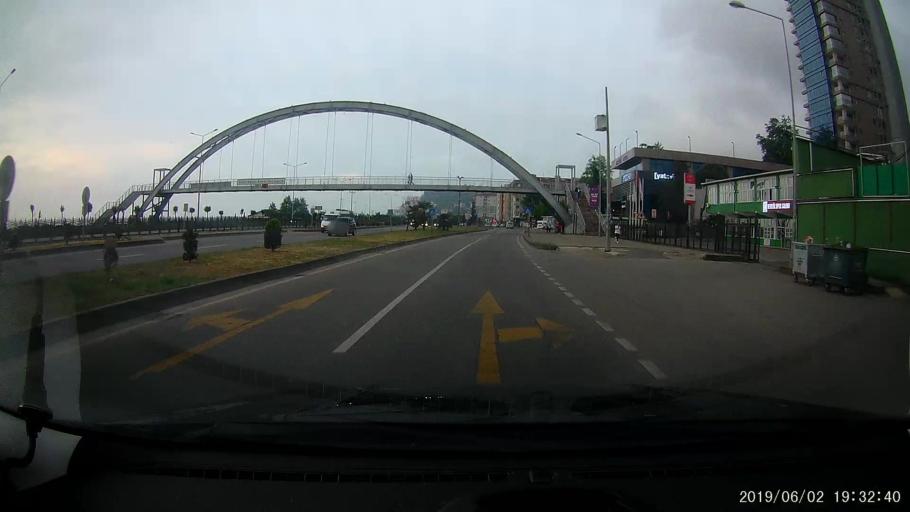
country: TR
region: Giresun
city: Giresun
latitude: 40.9106
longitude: 38.3715
